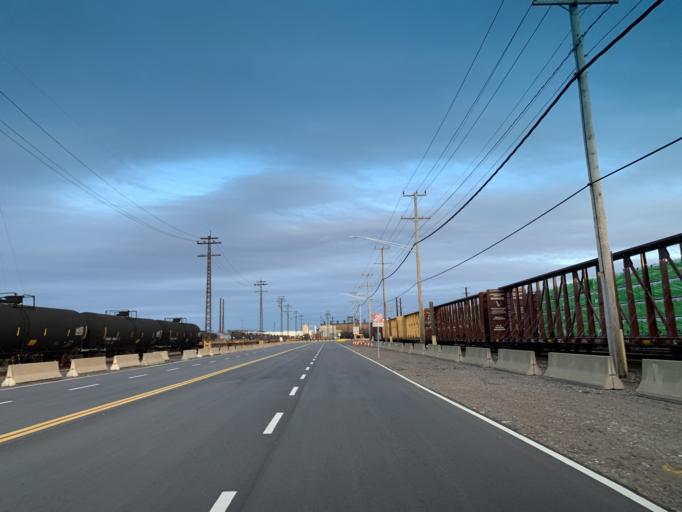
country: US
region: Maryland
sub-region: Baltimore County
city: Edgemere
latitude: 39.2265
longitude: -76.4851
